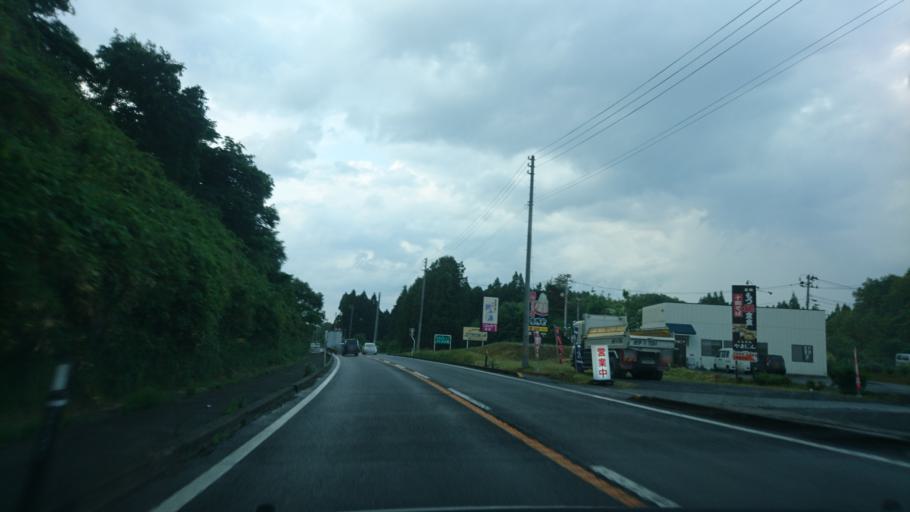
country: JP
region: Iwate
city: Ichinoseki
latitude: 38.9520
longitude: 141.1212
